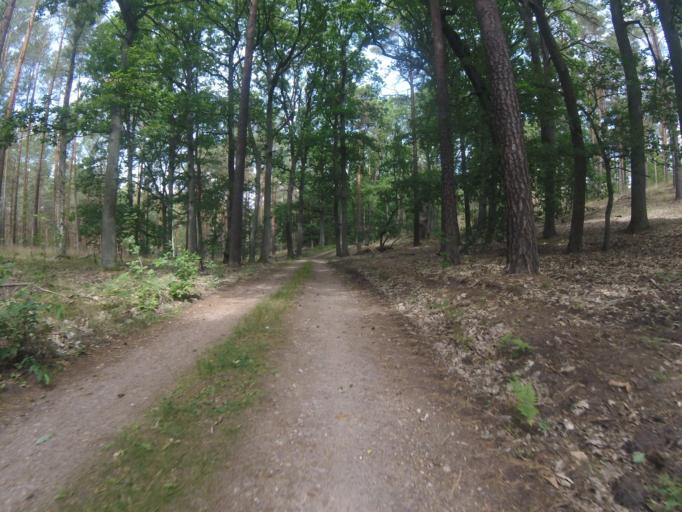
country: DE
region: Brandenburg
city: Gross Koris
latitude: 52.1985
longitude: 13.6744
